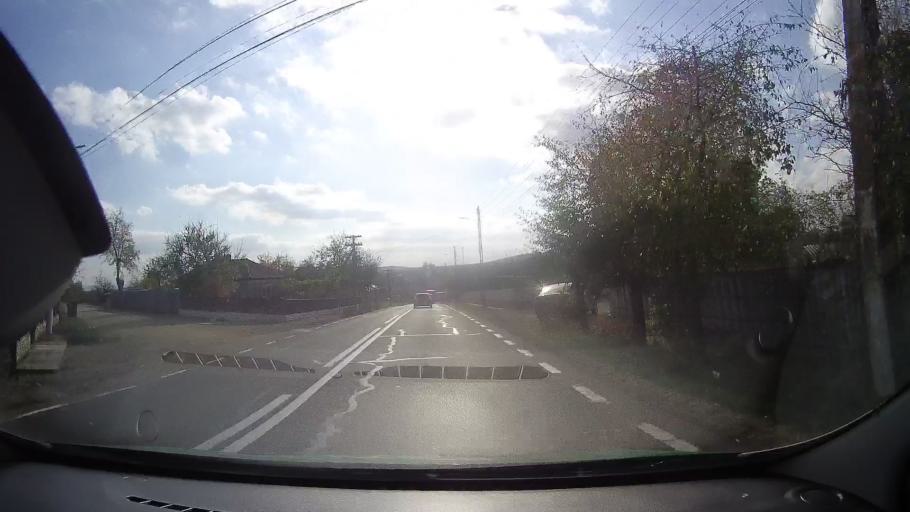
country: RO
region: Tulcea
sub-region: Comuna Nalbant
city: Nalbant
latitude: 45.0505
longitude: 28.6166
